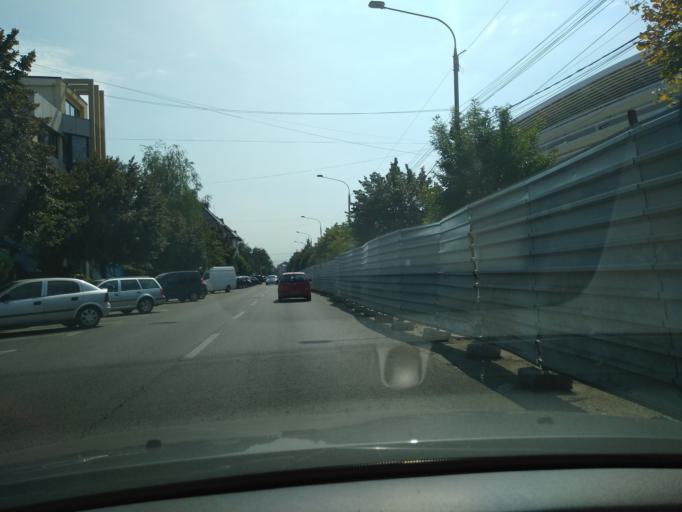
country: RO
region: Gorj
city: Targu Jiu
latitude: 45.0439
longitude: 23.2718
